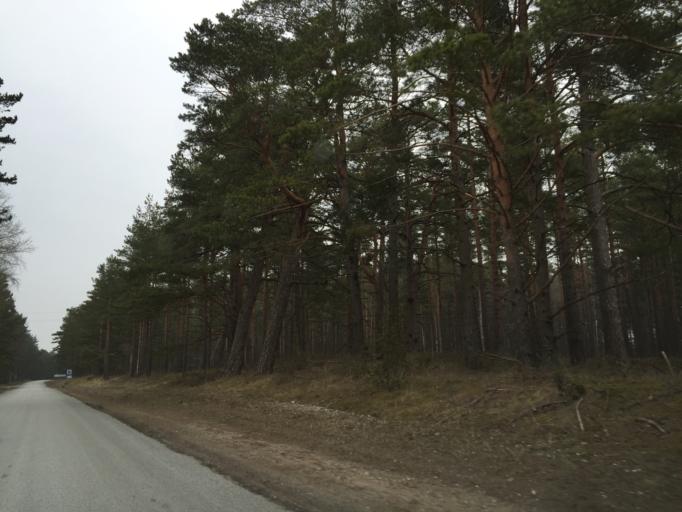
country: LV
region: Salacgrivas
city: Ainazi
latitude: 58.0296
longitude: 24.4592
